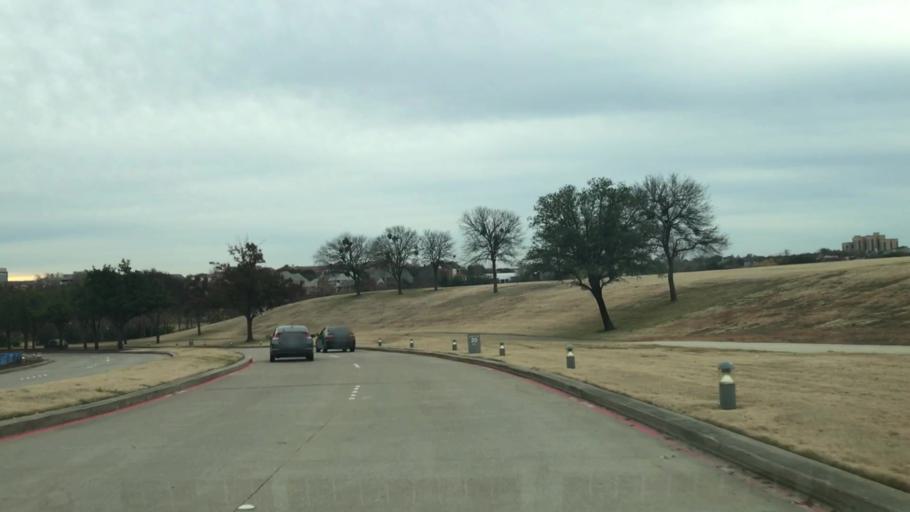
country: US
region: Texas
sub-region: Dallas County
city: Irving
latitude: 32.8761
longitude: -96.9565
